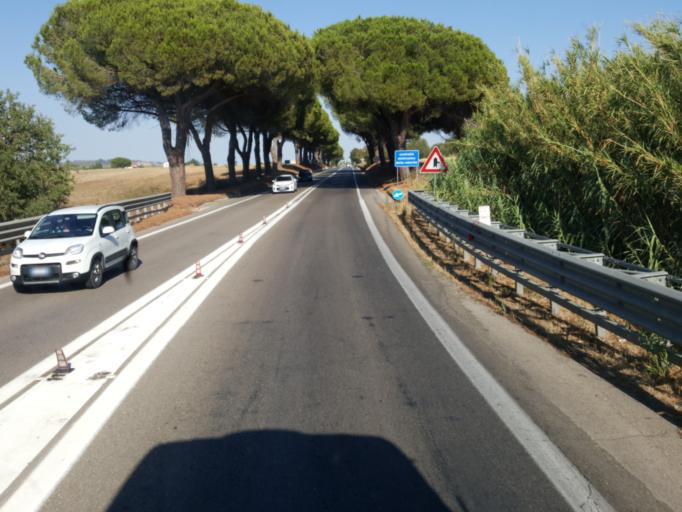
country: IT
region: Tuscany
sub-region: Provincia di Grosseto
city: Capalbio
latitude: 42.4146
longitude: 11.4127
